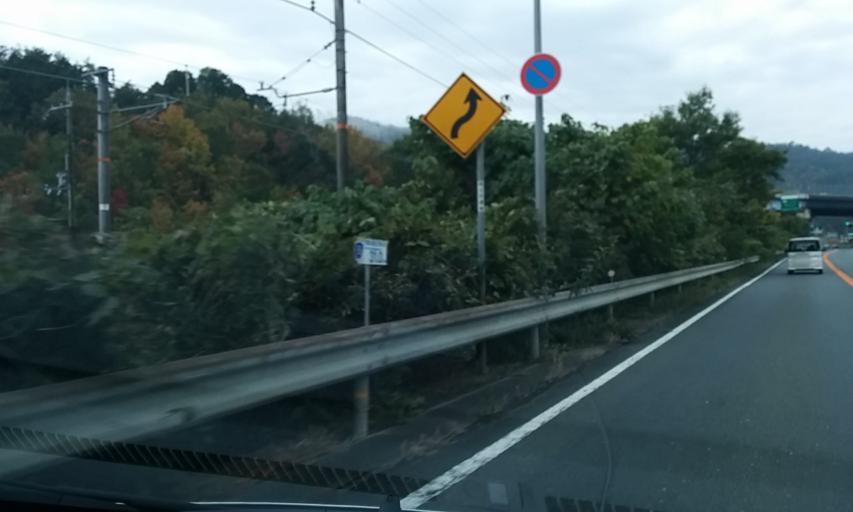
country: JP
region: Kyoto
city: Kameoka
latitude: 35.0821
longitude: 135.5123
